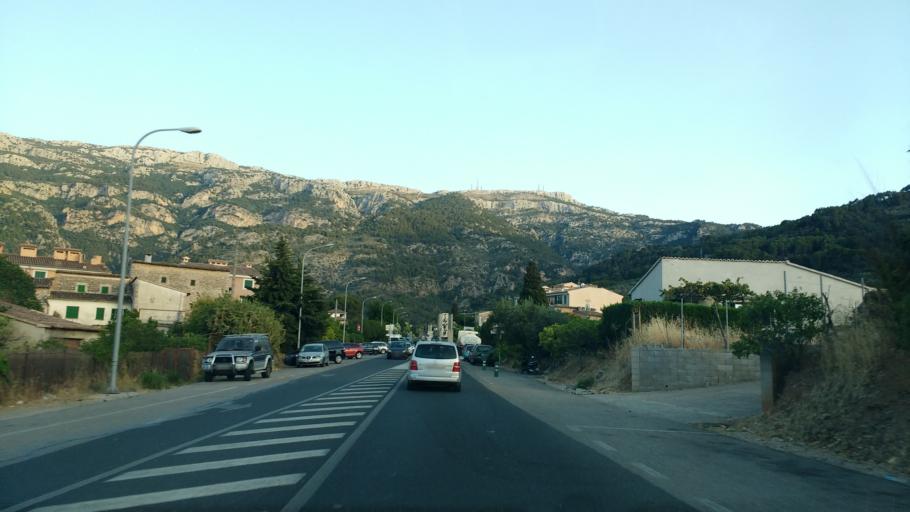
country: ES
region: Balearic Islands
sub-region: Illes Balears
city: Soller
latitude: 39.7723
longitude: 2.7057
